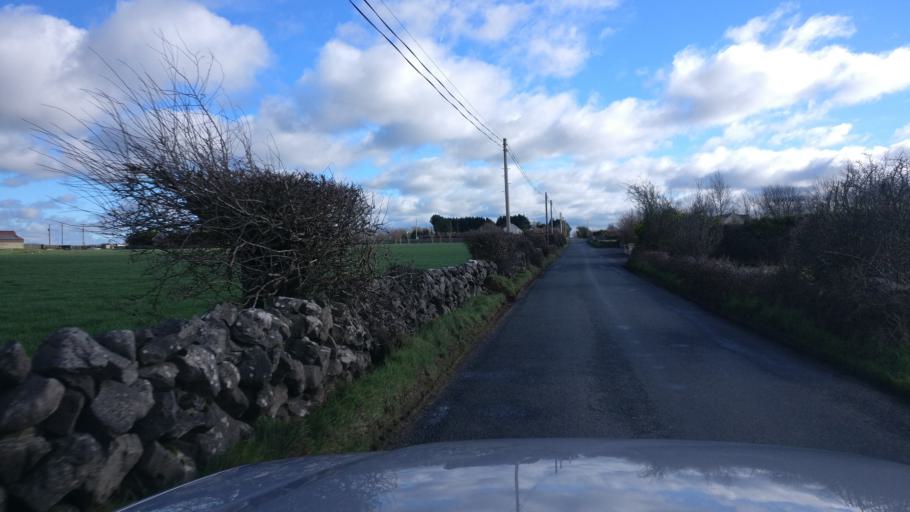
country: IE
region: Connaught
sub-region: County Galway
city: Oranmore
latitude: 53.2653
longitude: -8.8698
